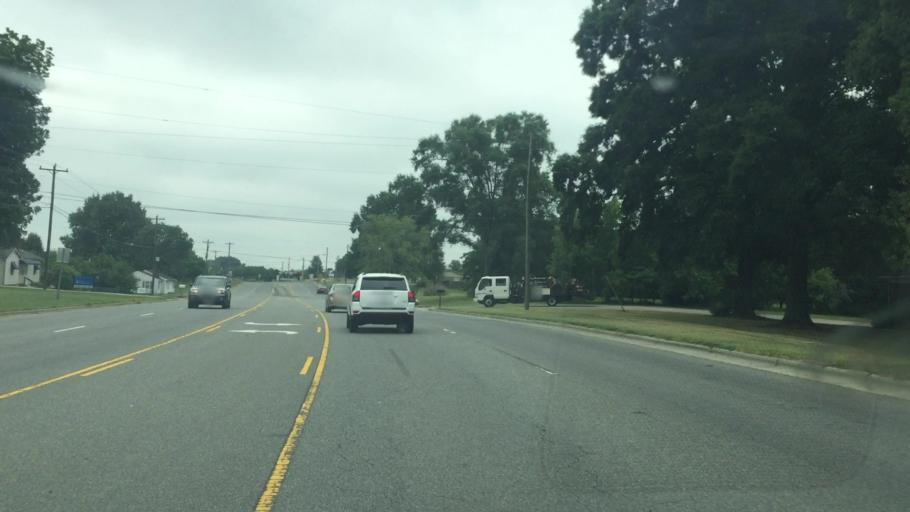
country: US
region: North Carolina
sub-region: Cabarrus County
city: Kannapolis
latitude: 35.4255
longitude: -80.6786
